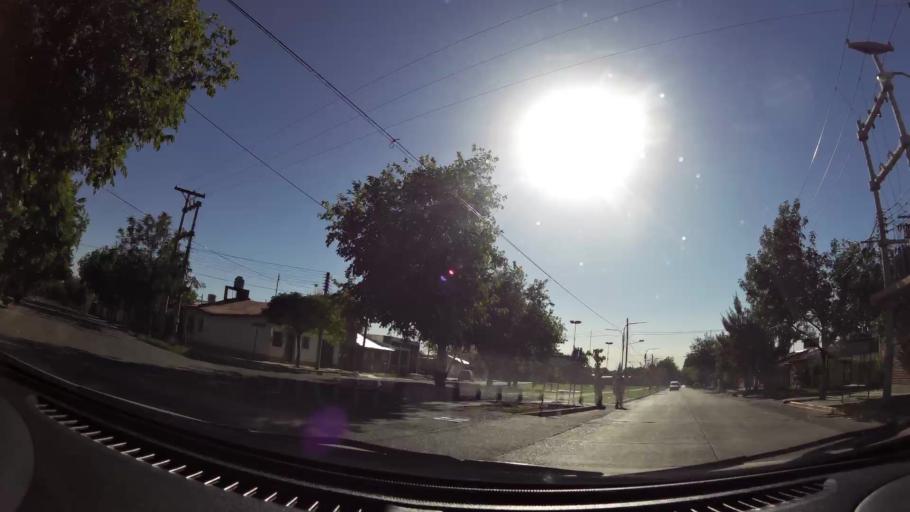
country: AR
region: Mendoza
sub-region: Departamento de Godoy Cruz
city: Godoy Cruz
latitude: -32.9290
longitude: -68.8670
